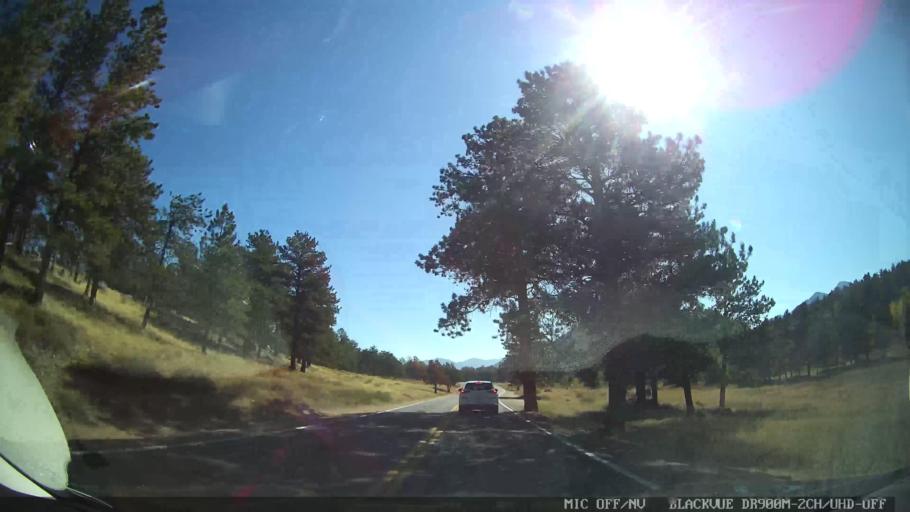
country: US
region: Colorado
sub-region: Larimer County
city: Estes Park
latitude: 40.3671
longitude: -105.5886
